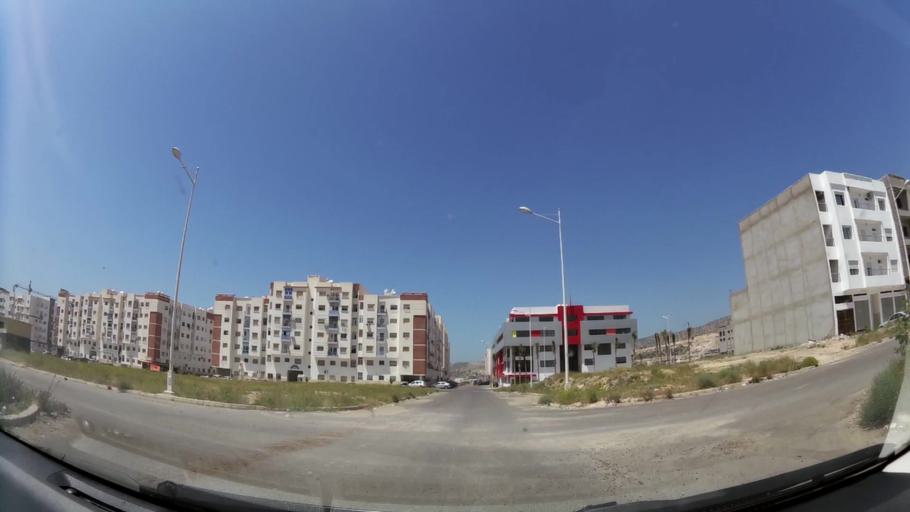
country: MA
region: Oued ed Dahab-Lagouira
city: Dakhla
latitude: 30.4401
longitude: -9.5625
